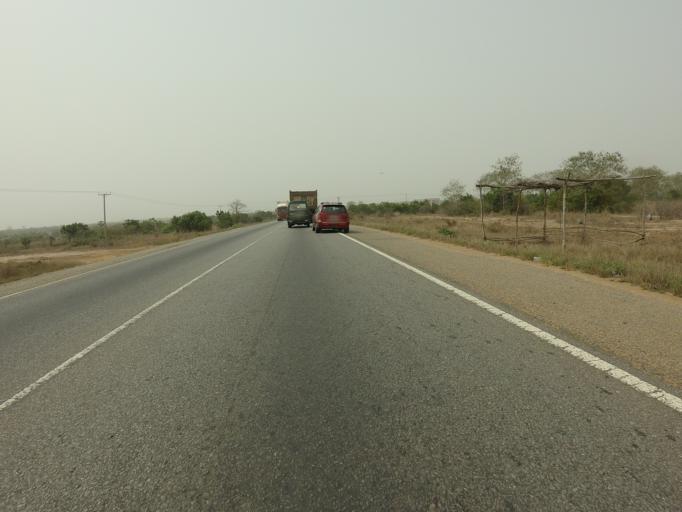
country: GH
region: Greater Accra
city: Tema
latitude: 5.8558
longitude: 0.2662
